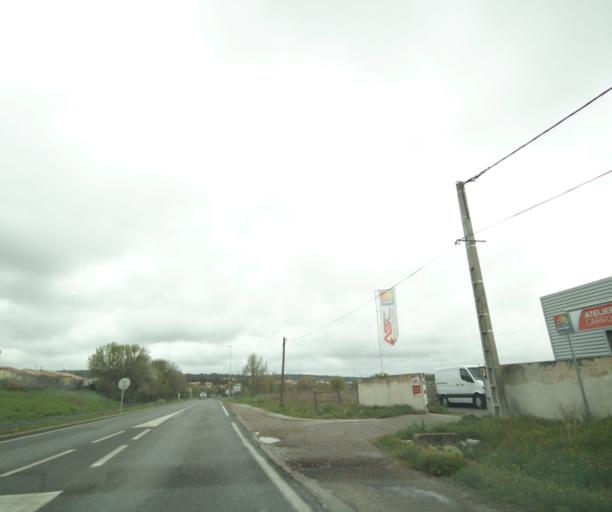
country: FR
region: Languedoc-Roussillon
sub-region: Departement de l'Herault
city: Cournonterral
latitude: 43.5582
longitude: 3.7288
